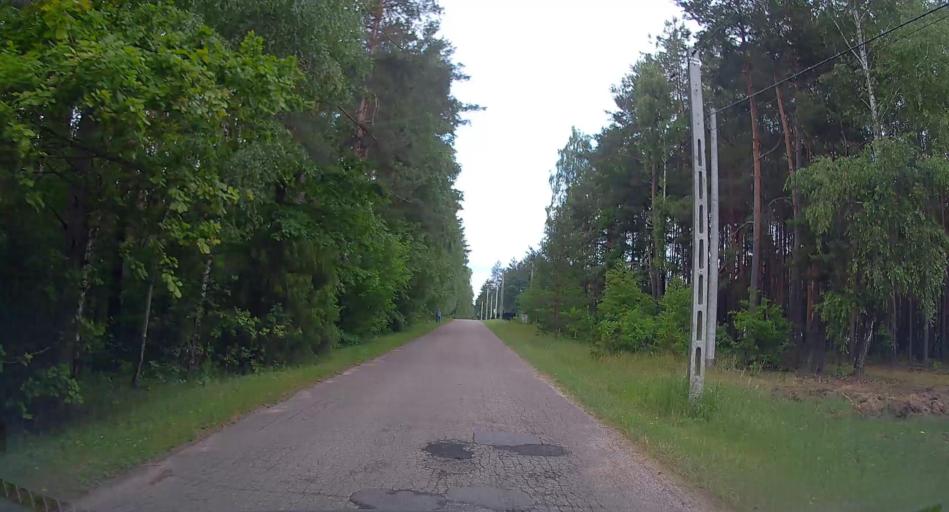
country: PL
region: Masovian Voivodeship
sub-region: Powiat ostrowski
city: Brok
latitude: 52.7421
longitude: 21.7416
